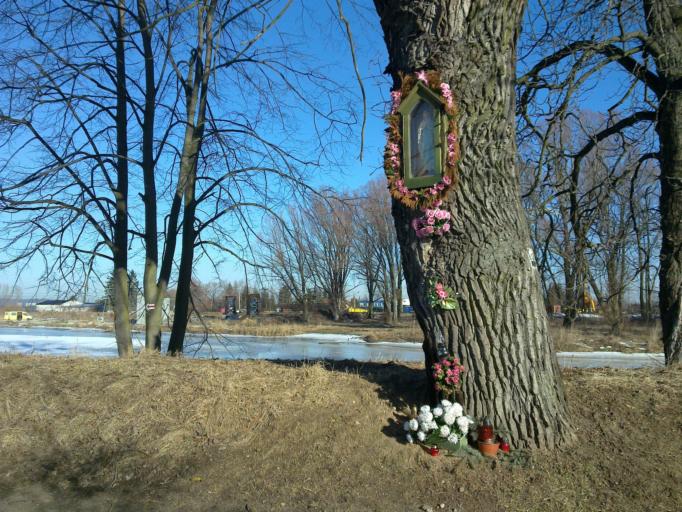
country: PL
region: Pomeranian Voivodeship
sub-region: Gdansk
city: Gdansk
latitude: 54.3131
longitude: 18.6877
